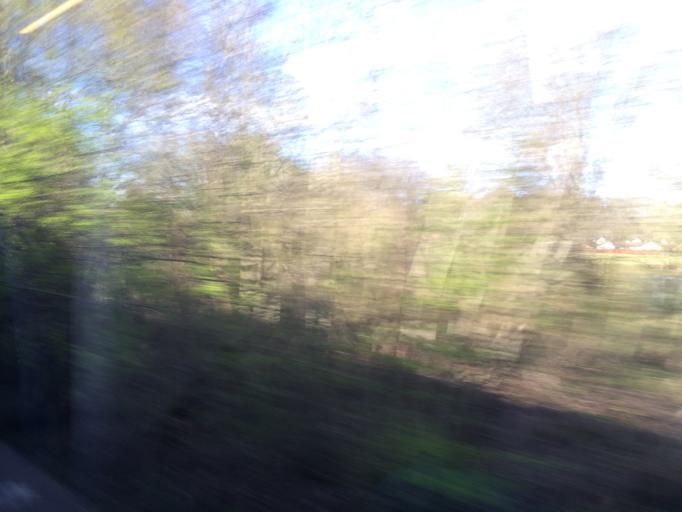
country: GB
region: Scotland
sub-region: Stirling
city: Bannockburn
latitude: 56.1008
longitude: -3.9129
